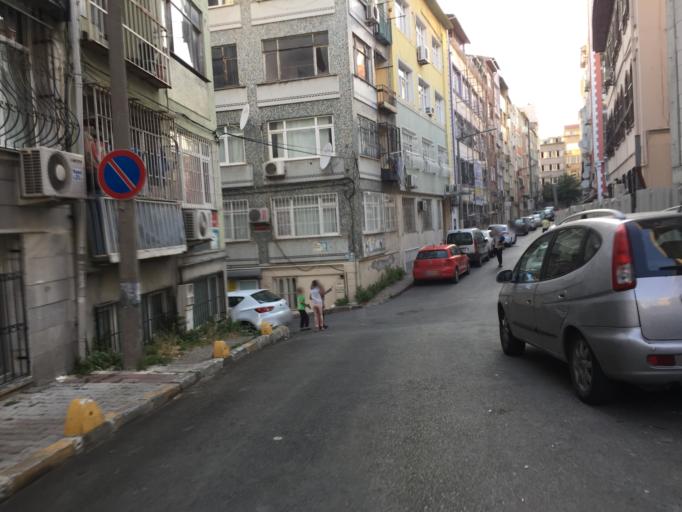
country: TR
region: Istanbul
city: Istanbul
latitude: 41.0164
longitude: 28.9477
